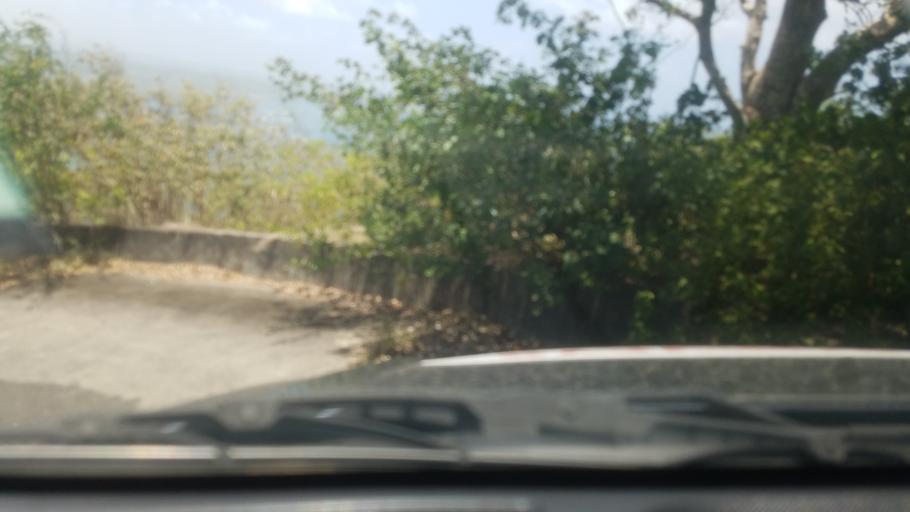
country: LC
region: Vieux-Fort
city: Vieux Fort
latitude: 13.7115
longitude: -60.9437
